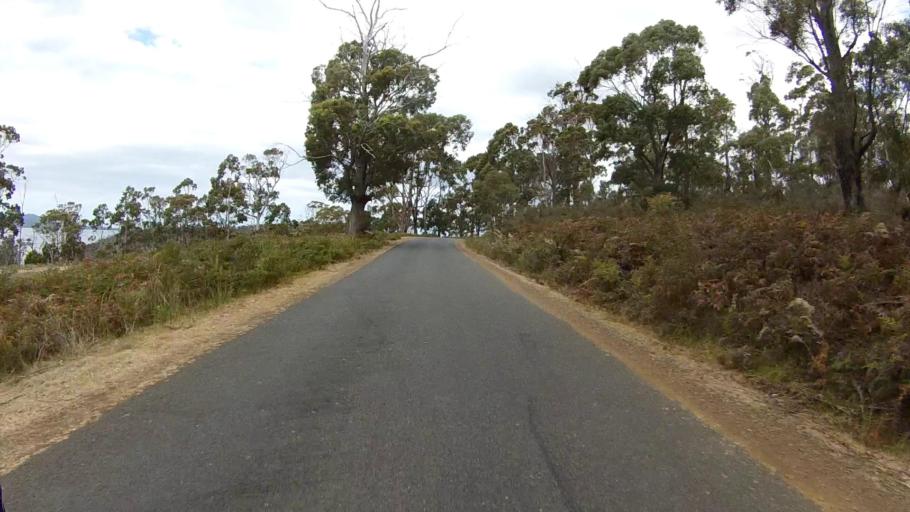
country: AU
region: Tasmania
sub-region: Sorell
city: Sorell
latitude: -42.5996
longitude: 147.9257
